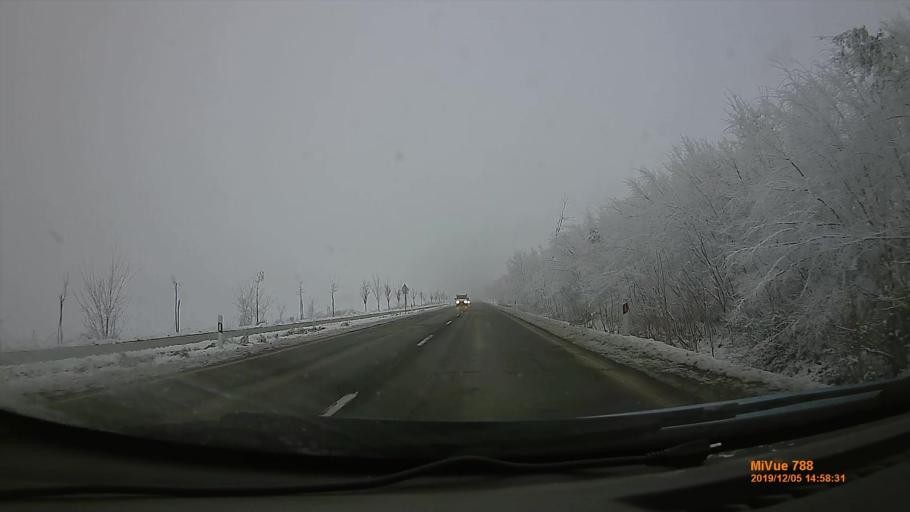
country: HU
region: Szabolcs-Szatmar-Bereg
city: Nyirtelek
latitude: 48.0491
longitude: 21.5704
